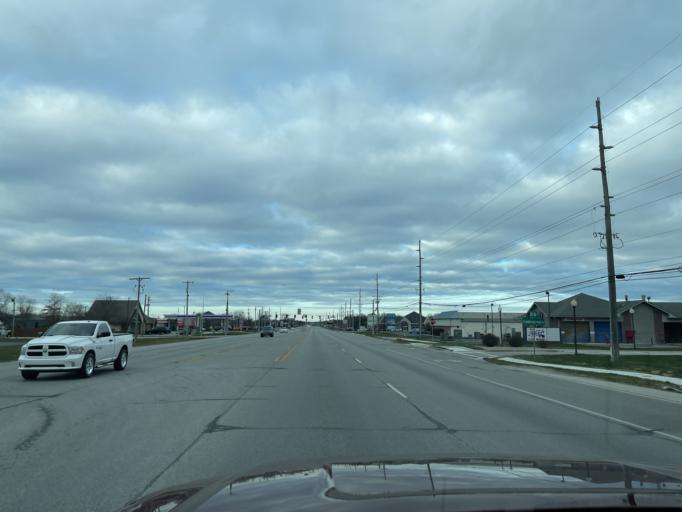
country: US
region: Indiana
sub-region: Hendricks County
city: Avon
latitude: 39.7630
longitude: -86.3844
